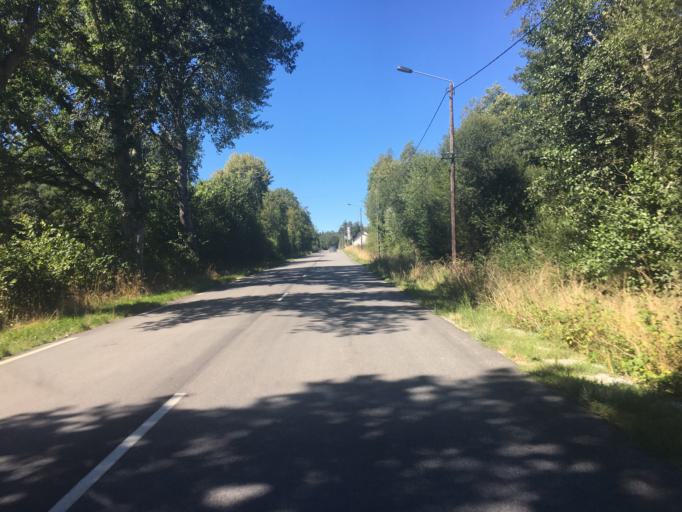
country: FR
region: Limousin
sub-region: Departement de la Correze
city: Bort-les-Orgues
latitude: 45.4301
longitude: 2.4551
